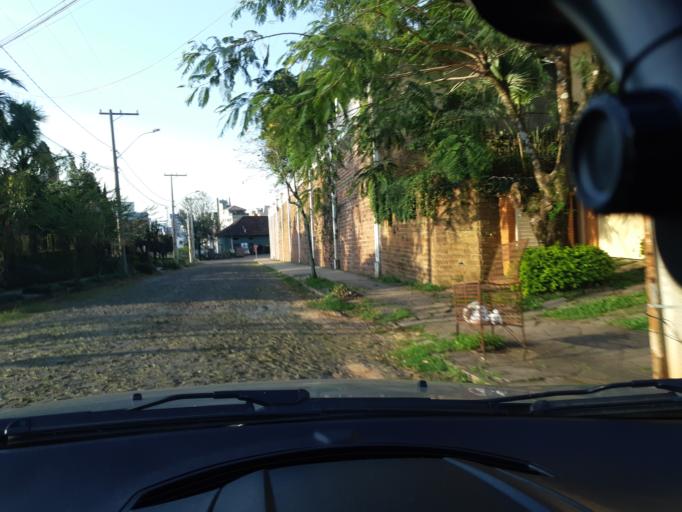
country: BR
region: Rio Grande do Sul
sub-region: Sao Leopoldo
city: Sao Leopoldo
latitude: -29.7736
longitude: -51.1400
